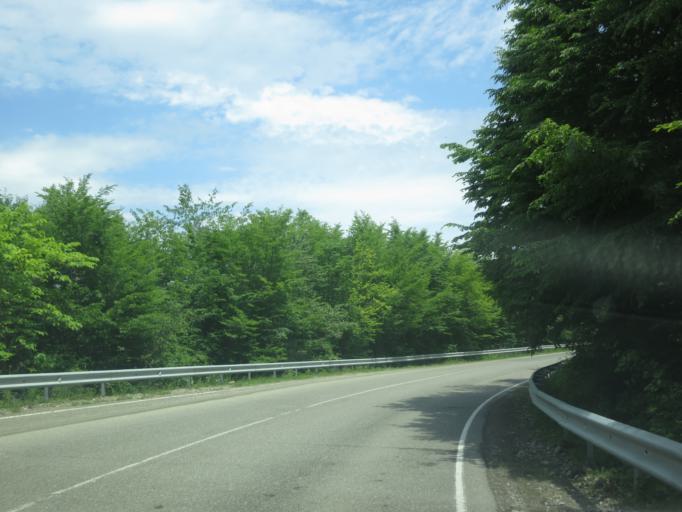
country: GE
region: Kakheti
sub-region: Telavi
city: Telavi
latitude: 41.8712
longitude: 45.3513
